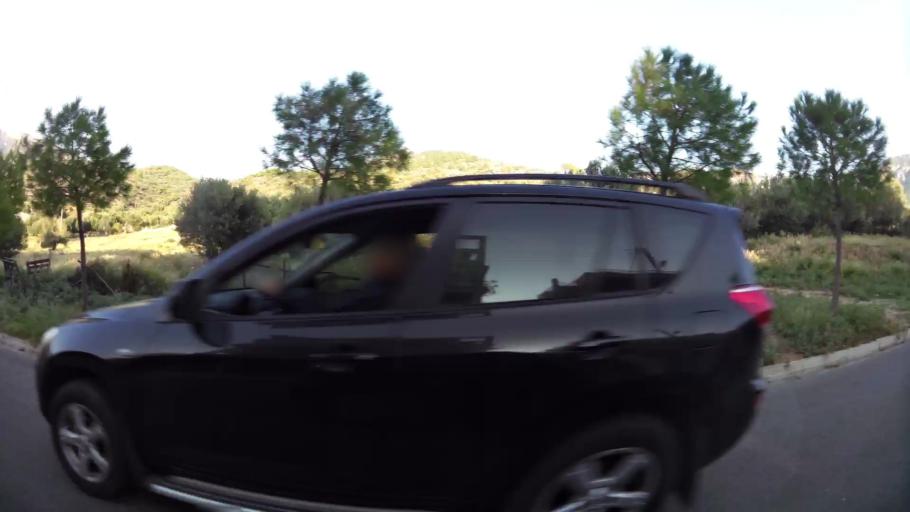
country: GR
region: Attica
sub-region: Nomarchia Athinas
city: Argyroupoli
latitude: 37.8951
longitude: 23.7755
